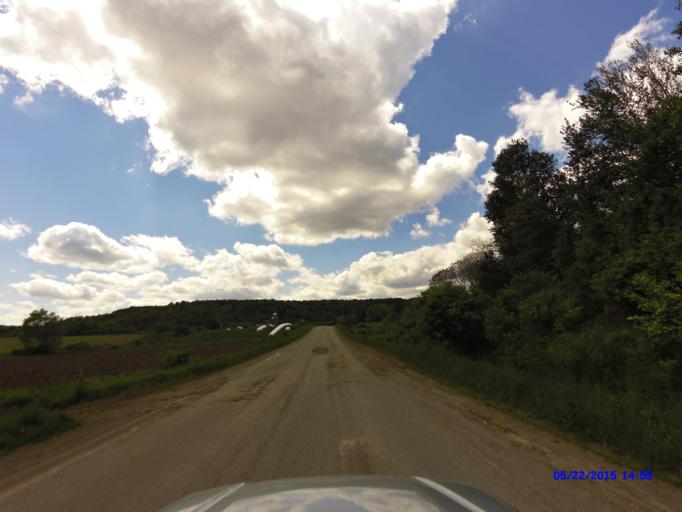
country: US
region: New York
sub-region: Cattaraugus County
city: Franklinville
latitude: 42.3778
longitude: -78.5986
